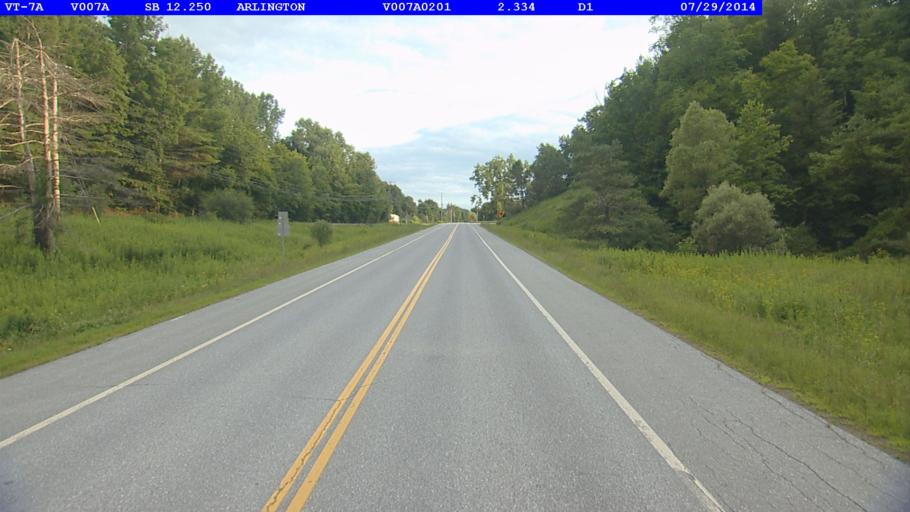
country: US
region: Vermont
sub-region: Bennington County
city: Arlington
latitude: 43.0536
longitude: -73.1634
